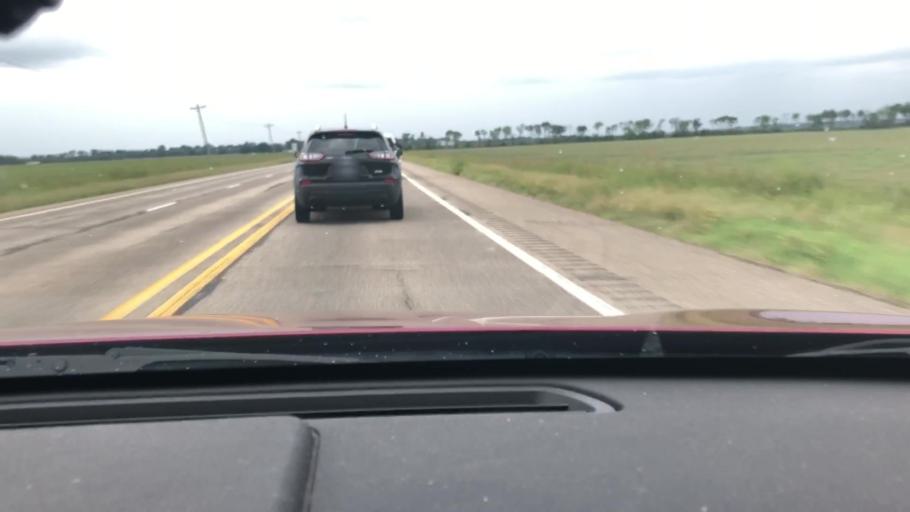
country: US
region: Arkansas
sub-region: Lafayette County
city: Lewisville
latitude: 33.3871
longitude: -93.7361
